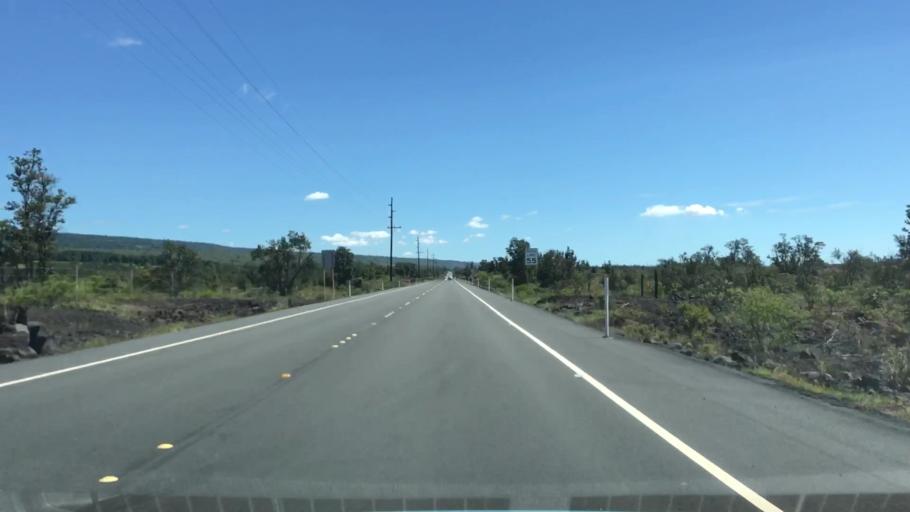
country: US
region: Hawaii
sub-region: Hawaii County
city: Pahala
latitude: 19.3095
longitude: -155.4121
